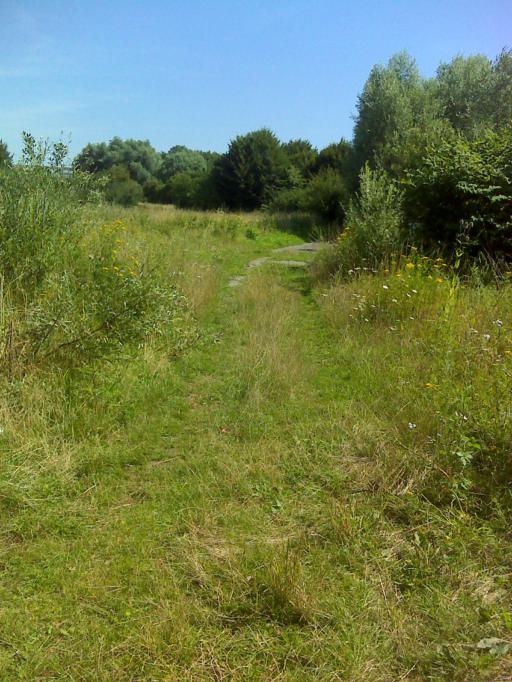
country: FR
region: Nord-Pas-de-Calais
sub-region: Departement du Nord
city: Berlaimont
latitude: 50.1921
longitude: 3.8152
